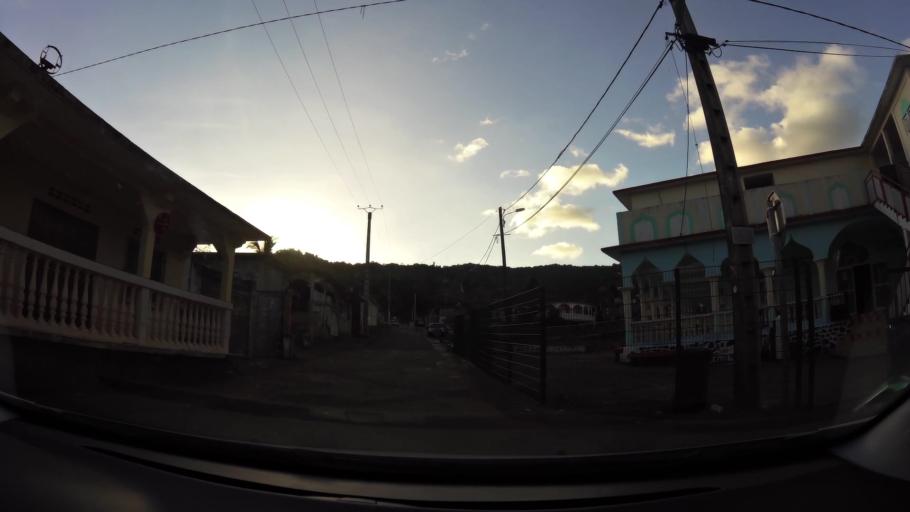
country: YT
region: Dembeni
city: Dembeni
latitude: -12.8369
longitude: 45.1719
